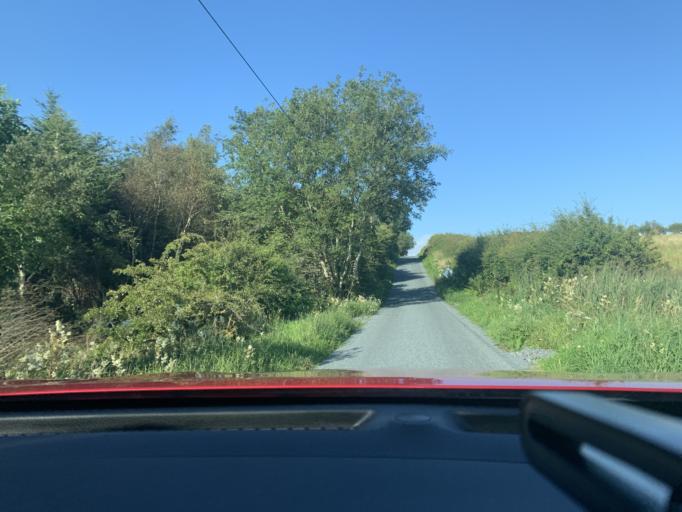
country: IE
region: Connaught
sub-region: Sligo
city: Tobercurry
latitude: 54.1429
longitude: -8.6854
